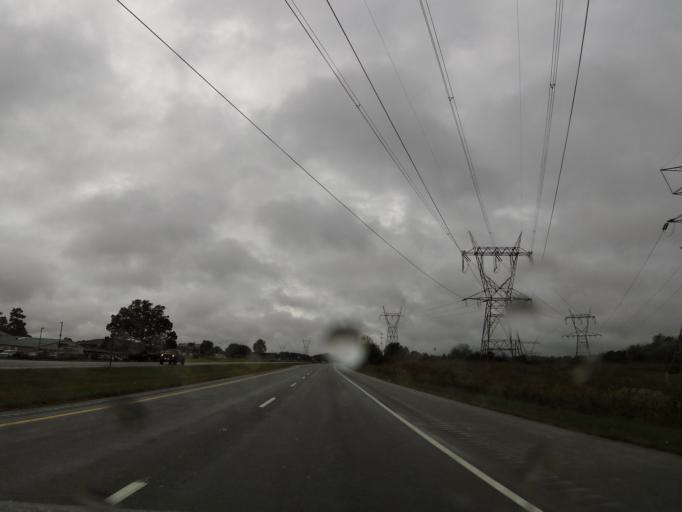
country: US
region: Tennessee
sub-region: Blount County
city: Maryville
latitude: 35.7547
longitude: -84.0151
